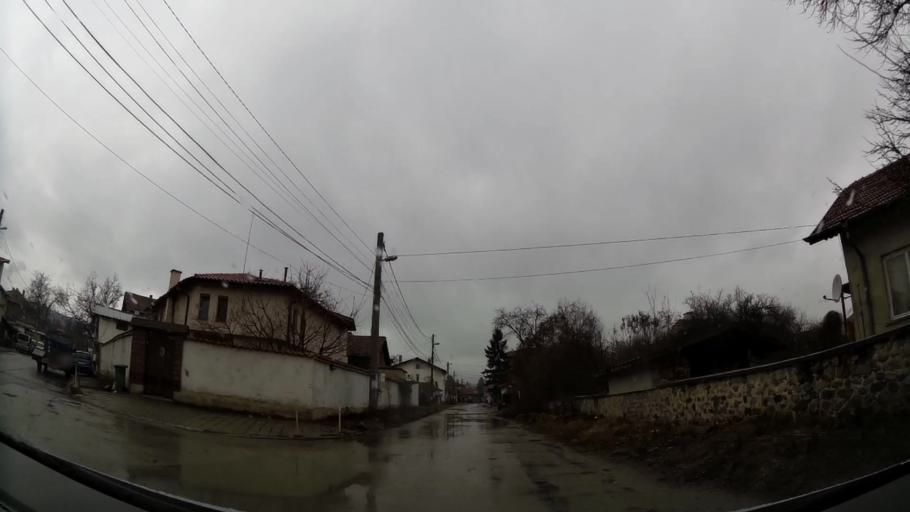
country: BG
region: Sofia-Capital
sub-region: Stolichna Obshtina
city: Sofia
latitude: 42.6271
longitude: 23.4120
